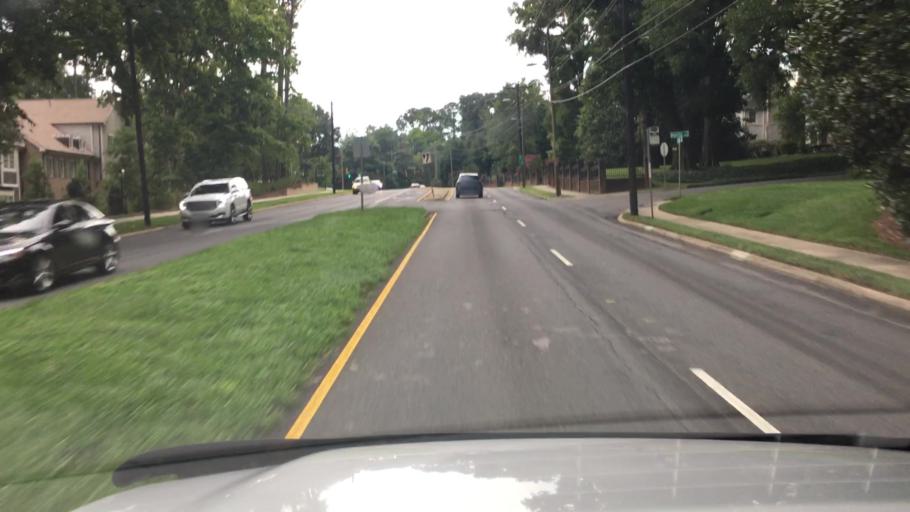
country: US
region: North Carolina
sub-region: Mecklenburg County
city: Charlotte
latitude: 35.1791
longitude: -80.8185
